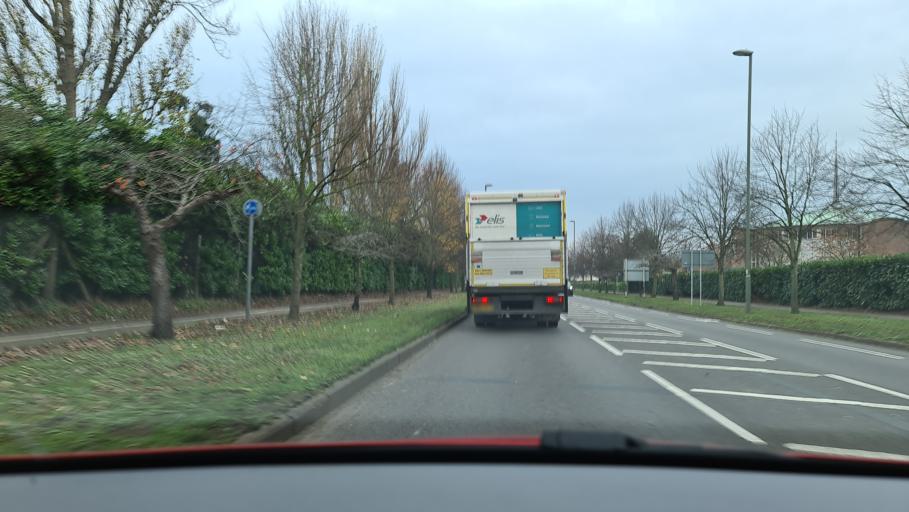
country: GB
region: England
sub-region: Surrey
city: Thames Ditton
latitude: 51.3894
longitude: -0.3458
